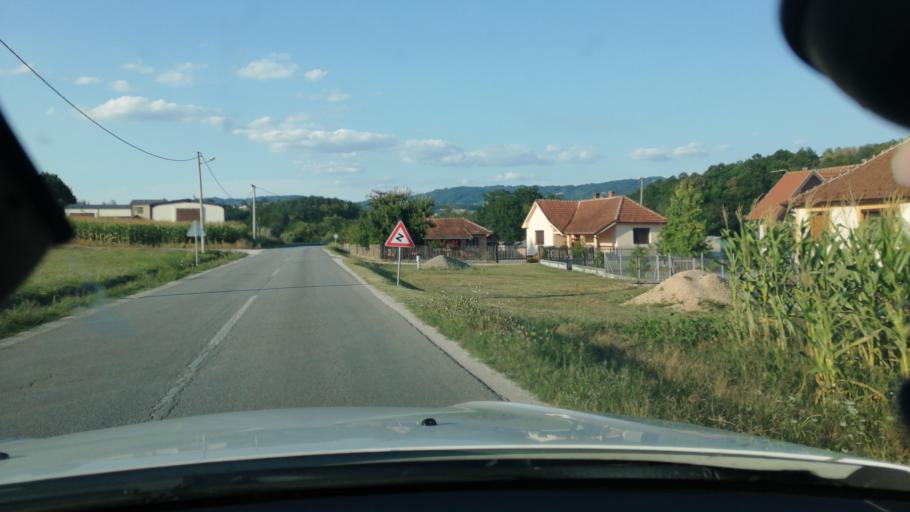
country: RS
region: Central Serbia
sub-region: Moravicki Okrug
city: Lucani
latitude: 43.7944
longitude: 20.2544
